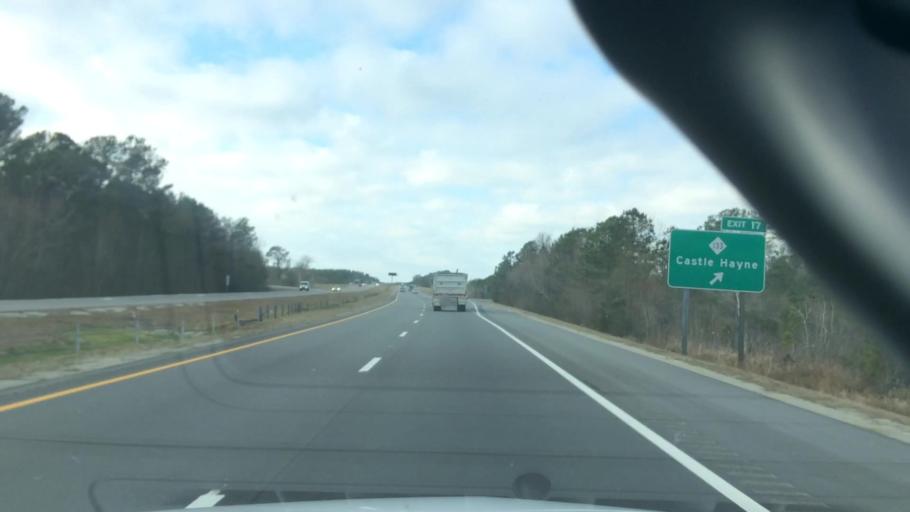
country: US
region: North Carolina
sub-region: New Hanover County
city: Wrightsboro
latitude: 34.3157
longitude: -77.9149
